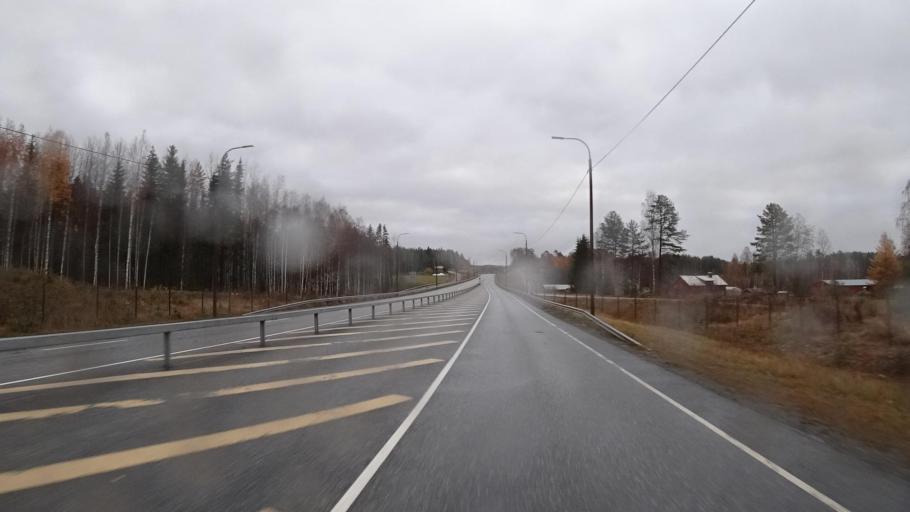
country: FI
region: Southern Savonia
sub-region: Savonlinna
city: Heinaevesi
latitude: 62.5013
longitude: 28.3963
